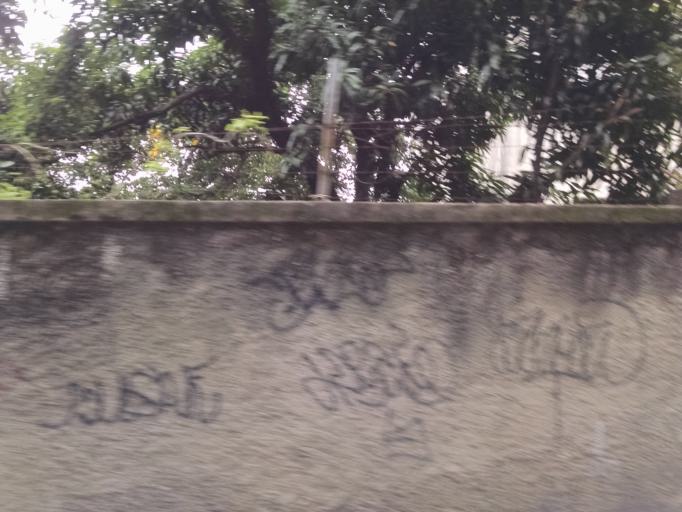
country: BR
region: Rio de Janeiro
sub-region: Rio De Janeiro
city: Rio de Janeiro
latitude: -22.9276
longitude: -43.1935
